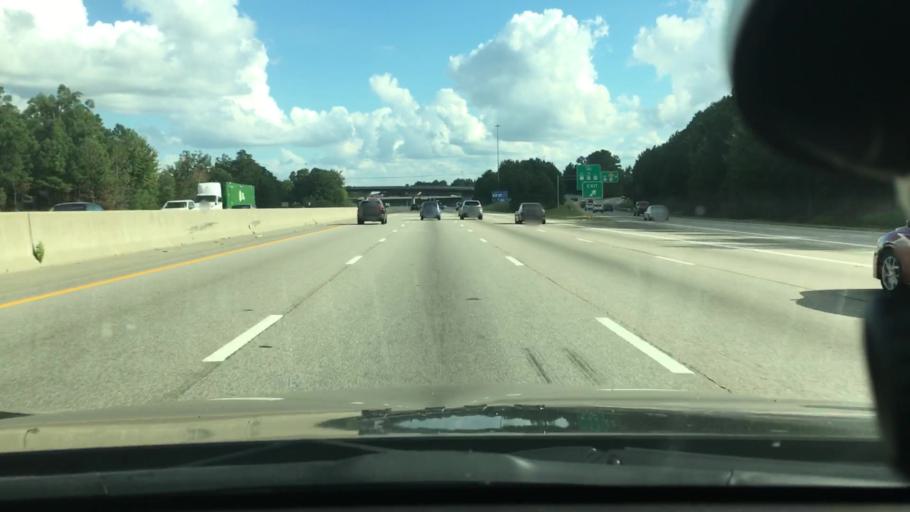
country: US
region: North Carolina
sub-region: Wake County
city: Morrisville
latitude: 35.8777
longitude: -78.8356
